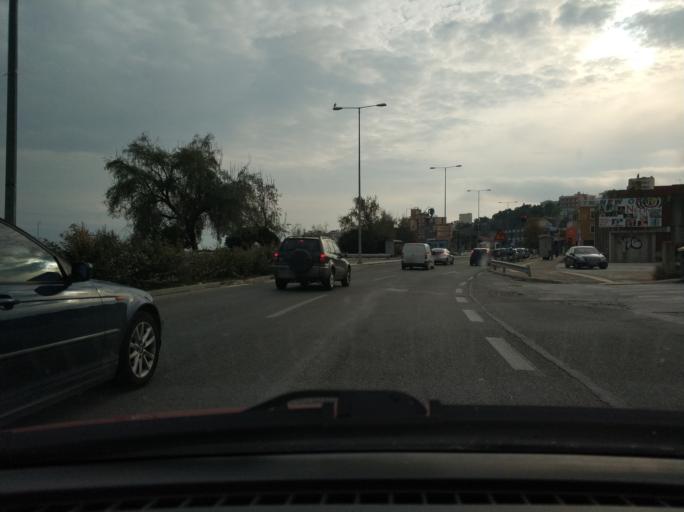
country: GR
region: East Macedonia and Thrace
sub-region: Nomos Kavalas
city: Kavala
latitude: 40.9298
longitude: 24.3915
